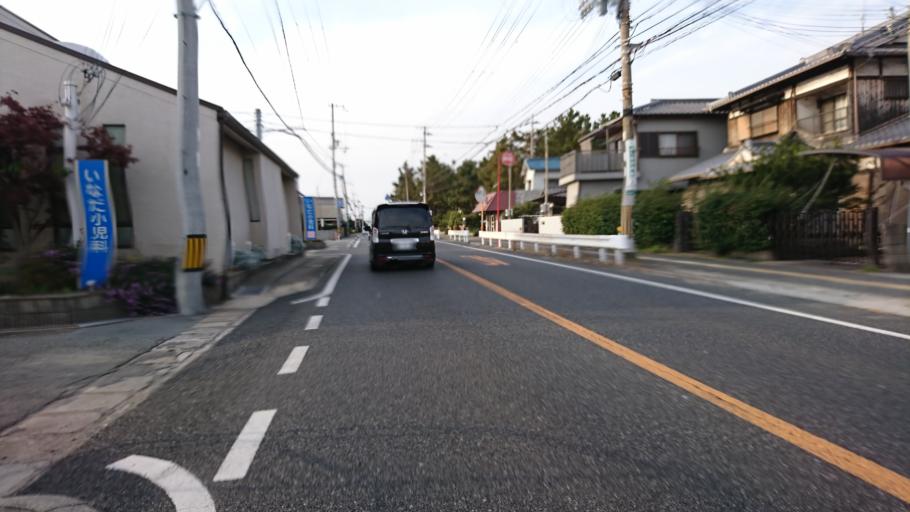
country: JP
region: Hyogo
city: Kakogawacho-honmachi
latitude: 34.7327
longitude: 134.8334
